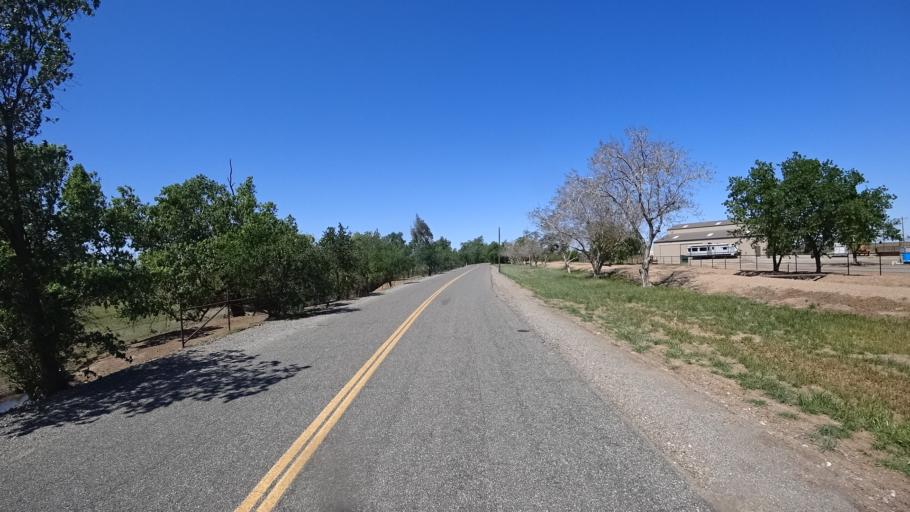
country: US
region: California
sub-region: Glenn County
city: Orland
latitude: 39.7890
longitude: -122.2238
